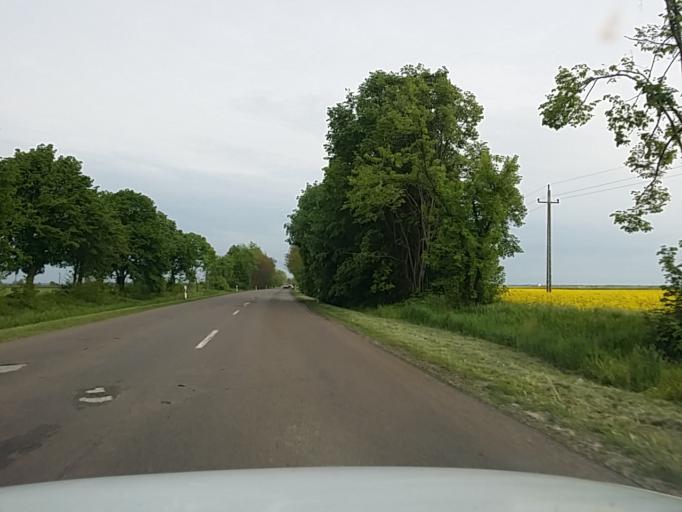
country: HU
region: Pest
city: Szentlorinckata
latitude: 47.5396
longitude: 19.8263
